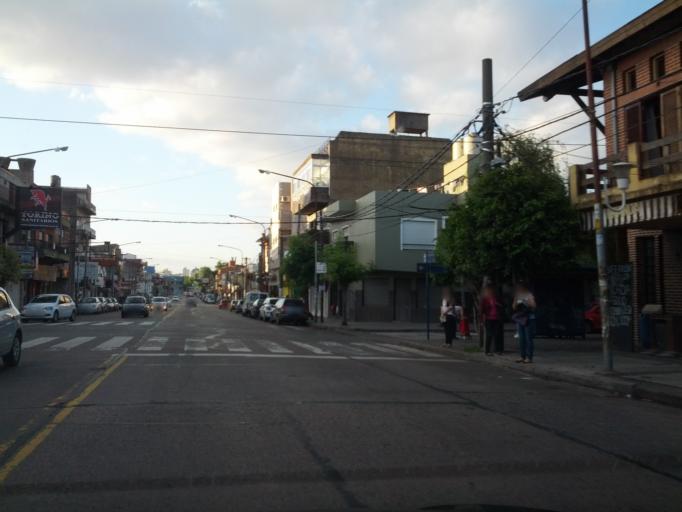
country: AR
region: Buenos Aires
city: San Justo
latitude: -34.6550
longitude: -58.5492
